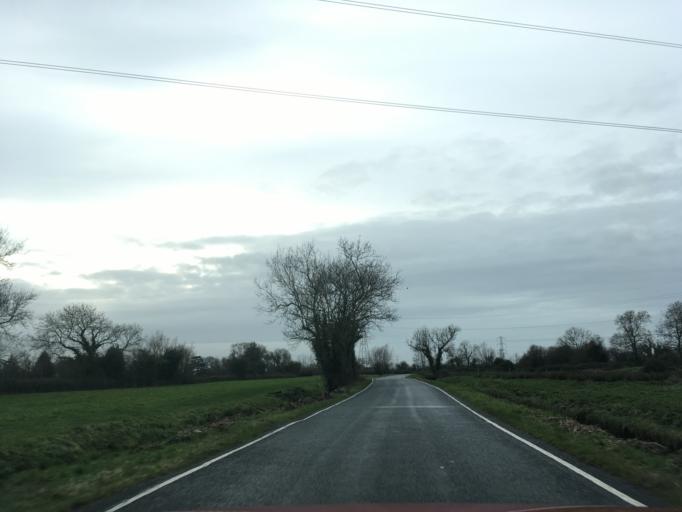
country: GB
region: Wales
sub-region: Newport
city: Goldcliff
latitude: 51.5635
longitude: -2.9063
